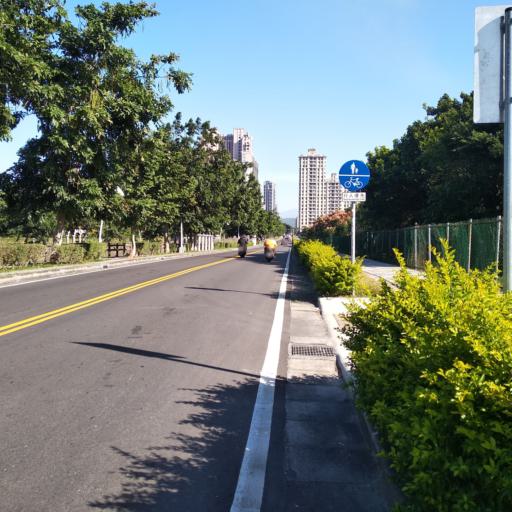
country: TW
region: Taiwan
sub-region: Hsinchu
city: Zhubei
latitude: 24.8283
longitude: 121.0207
